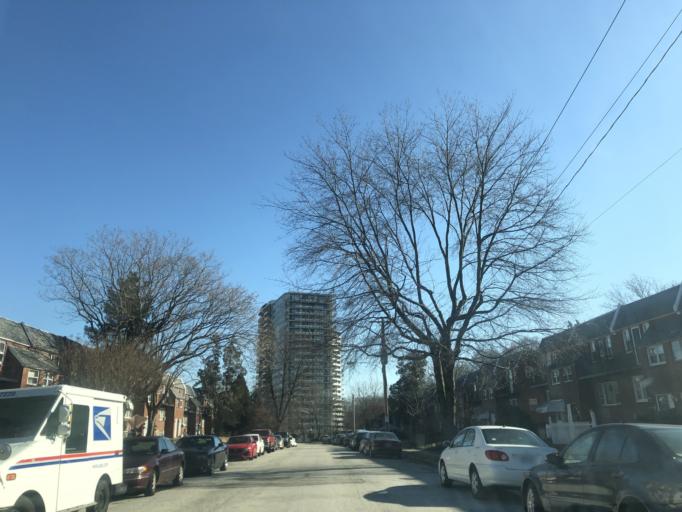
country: US
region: Pennsylvania
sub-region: Montgomery County
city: Bala-Cynwyd
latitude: 39.9993
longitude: -75.2116
